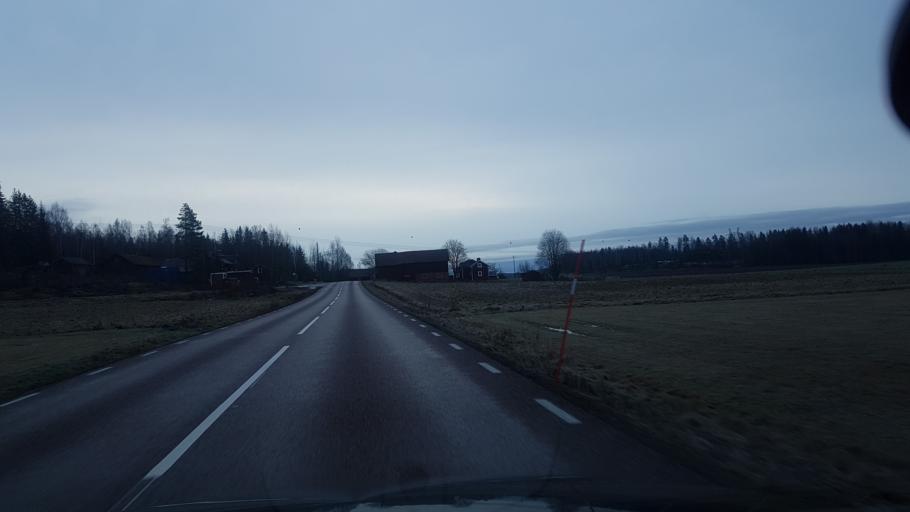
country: SE
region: Dalarna
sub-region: Saters Kommun
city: Saeter
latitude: 60.4179
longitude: 15.6717
